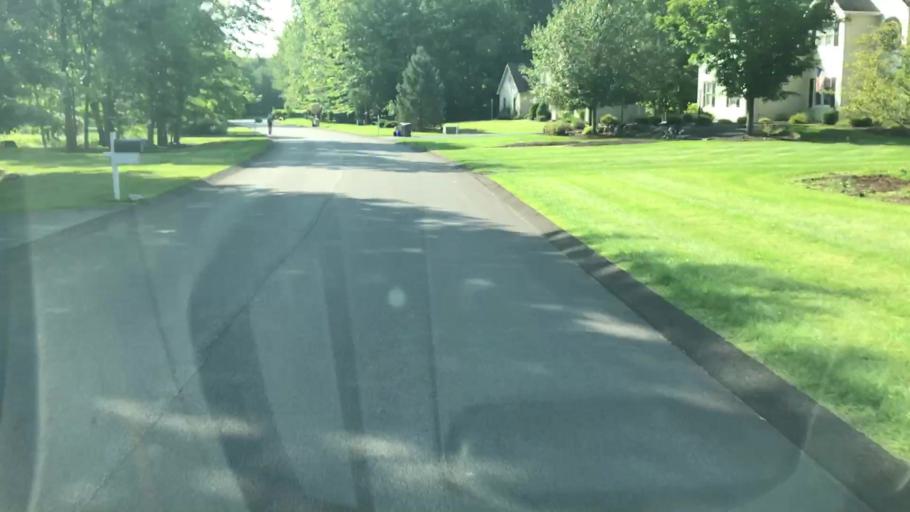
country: US
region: New York
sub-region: Onondaga County
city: Manlius
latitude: 42.9886
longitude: -75.9775
